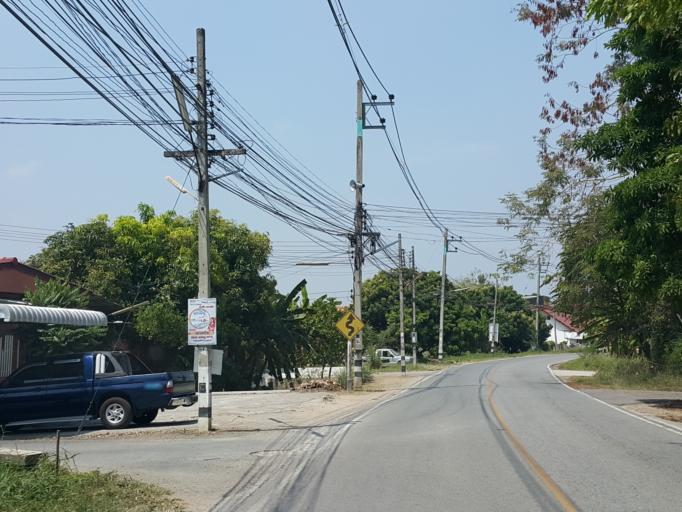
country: TH
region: Chiang Mai
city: Chiang Mai
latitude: 18.7423
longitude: 98.9901
